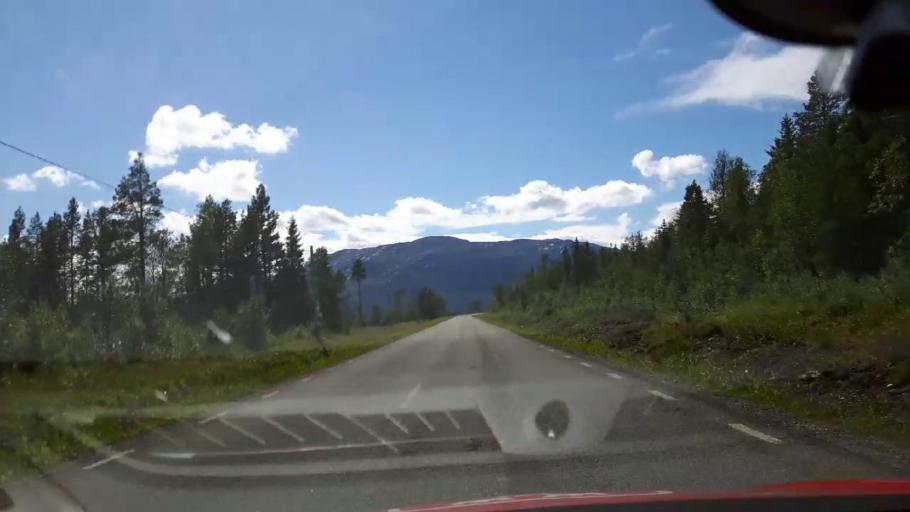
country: SE
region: Jaemtland
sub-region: Are Kommun
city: Are
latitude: 63.2199
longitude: 13.0944
